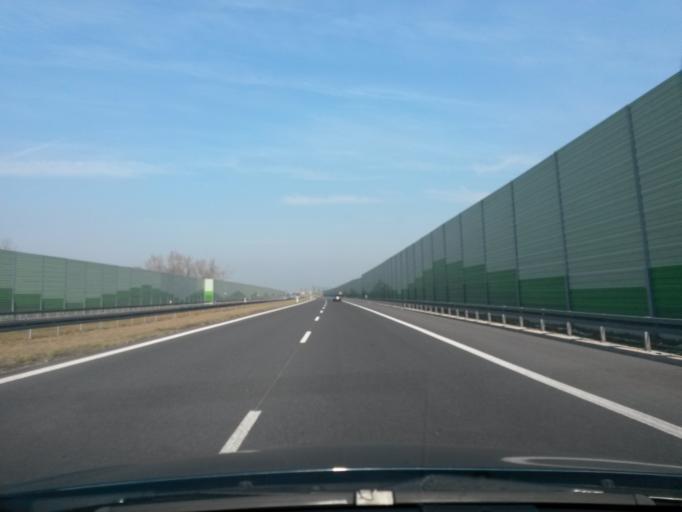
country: PL
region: Lodz Voivodeship
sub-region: Powiat leczycki
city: Piatek
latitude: 52.1163
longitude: 19.5041
